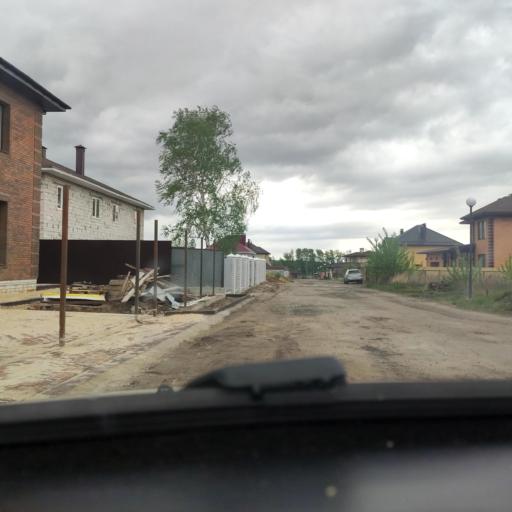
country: RU
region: Voronezj
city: Podgornoye
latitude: 51.7556
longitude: 39.1418
